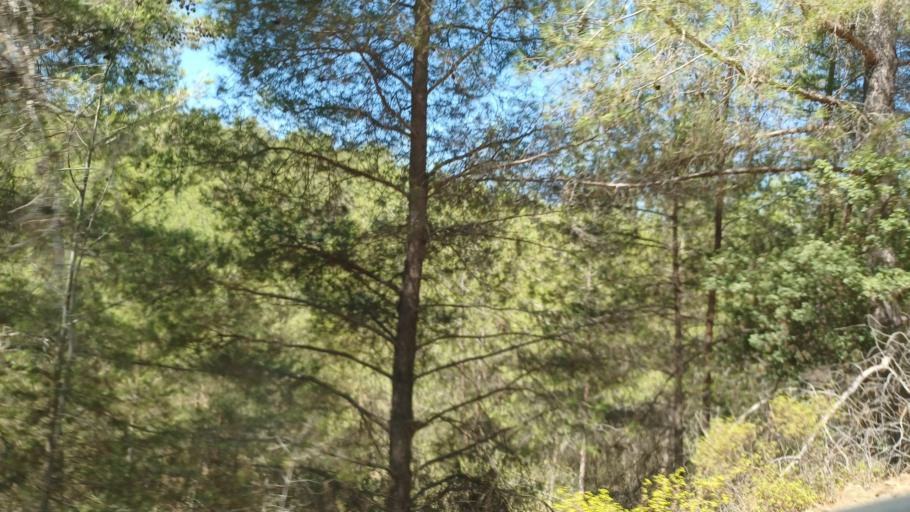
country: CY
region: Pafos
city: Mesogi
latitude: 34.9293
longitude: 32.6331
